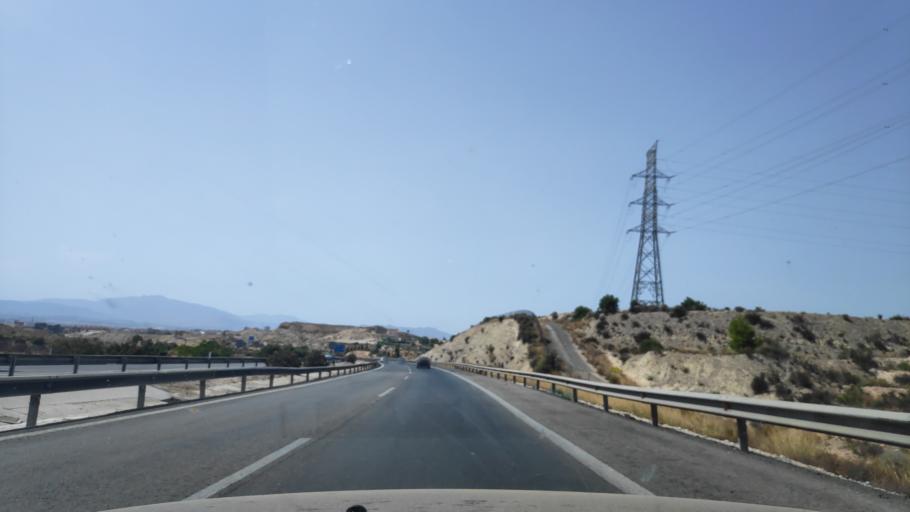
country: ES
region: Murcia
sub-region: Murcia
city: Molina de Segura
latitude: 38.0518
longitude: -1.1763
